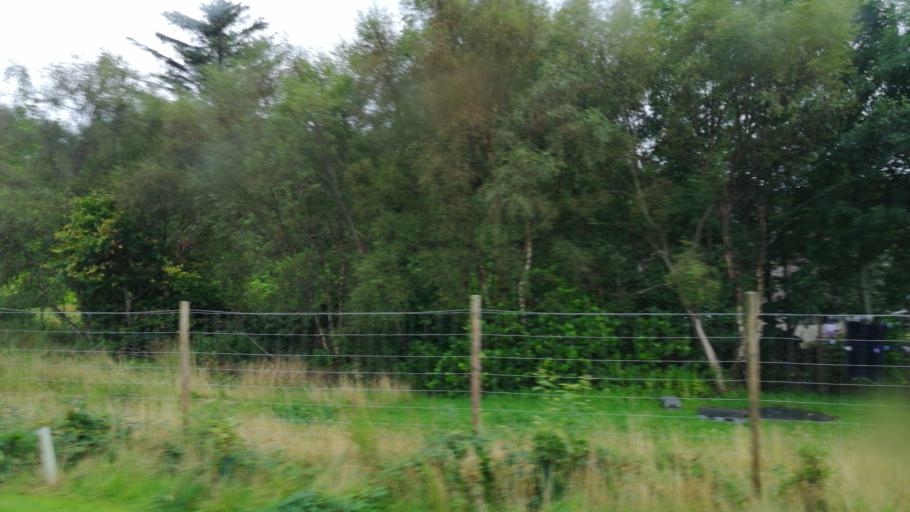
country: GB
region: Scotland
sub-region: Argyll and Bute
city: Isle Of Mull
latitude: 56.4793
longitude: -5.7151
